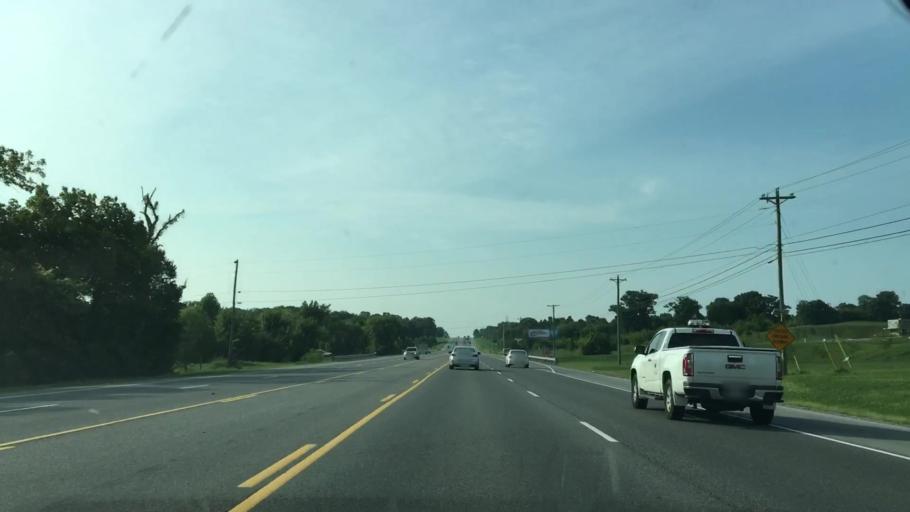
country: US
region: Tennessee
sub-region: Wilson County
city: Mount Juliet
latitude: 36.2209
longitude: -86.4245
